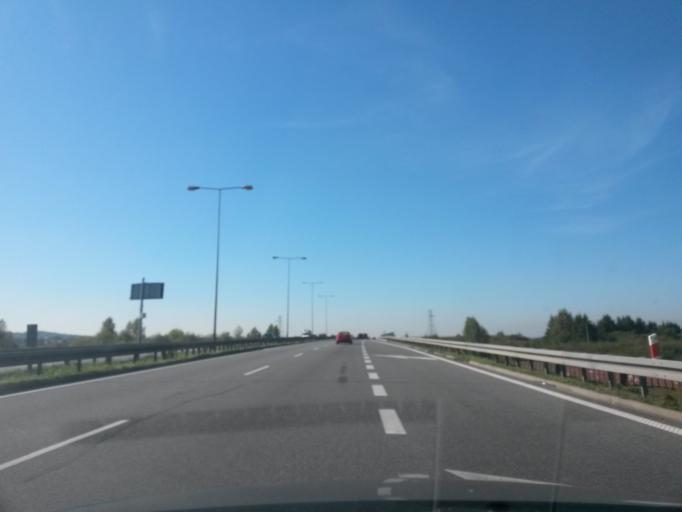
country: PL
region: Lesser Poland Voivodeship
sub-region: Powiat krakowski
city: Libertow
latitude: 49.9913
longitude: 19.9078
